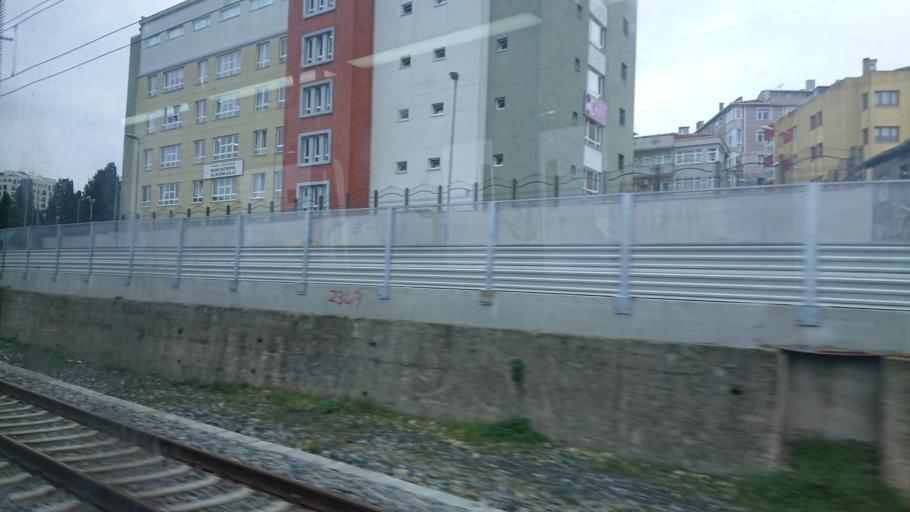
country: TR
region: Istanbul
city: Mahmutbey
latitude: 41.0023
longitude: 28.7696
